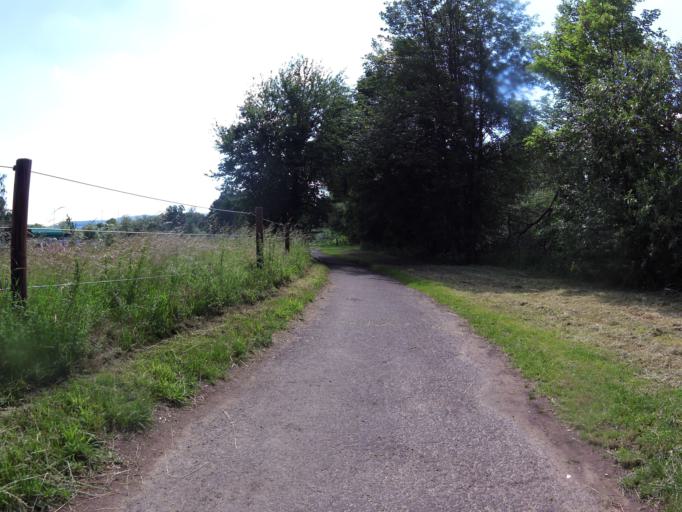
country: DE
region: Hesse
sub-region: Regierungsbezirk Kassel
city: Bad Hersfeld
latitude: 50.8611
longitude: 9.7033
